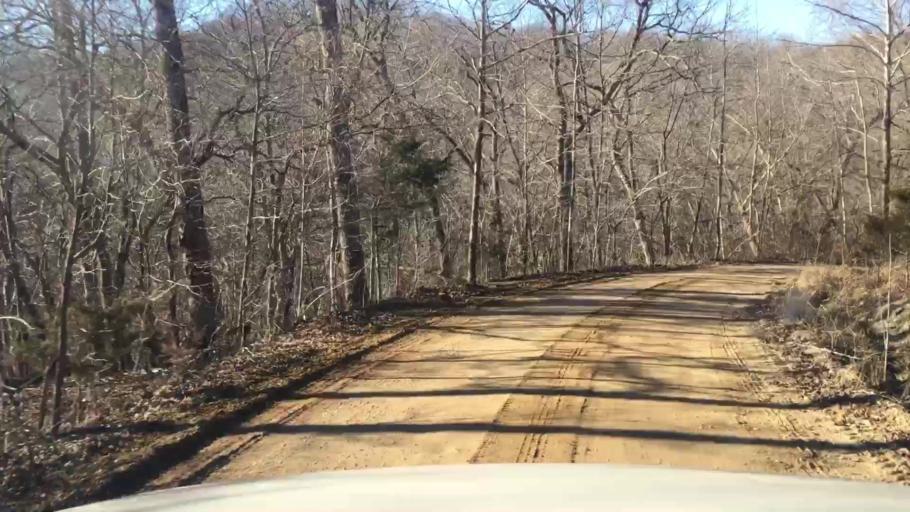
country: US
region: Missouri
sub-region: Camden County
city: Four Seasons
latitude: 38.3204
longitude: -92.7636
